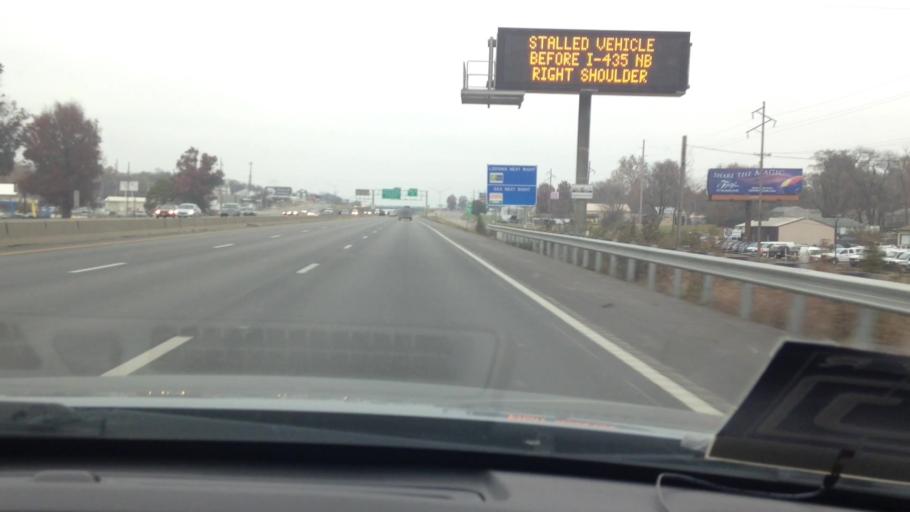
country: US
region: Missouri
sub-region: Jackson County
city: Grandview
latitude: 38.8795
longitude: -94.5257
